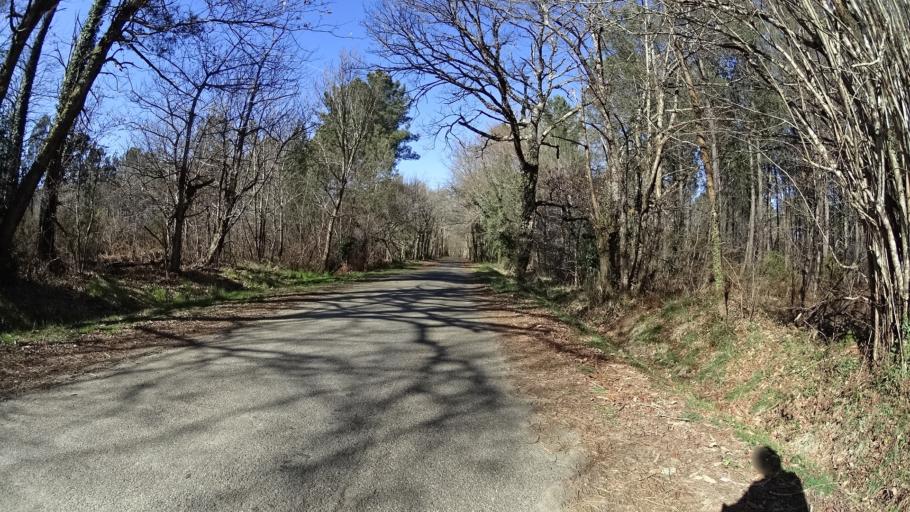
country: FR
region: Aquitaine
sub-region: Departement des Landes
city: Mees
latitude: 43.7436
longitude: -1.0969
